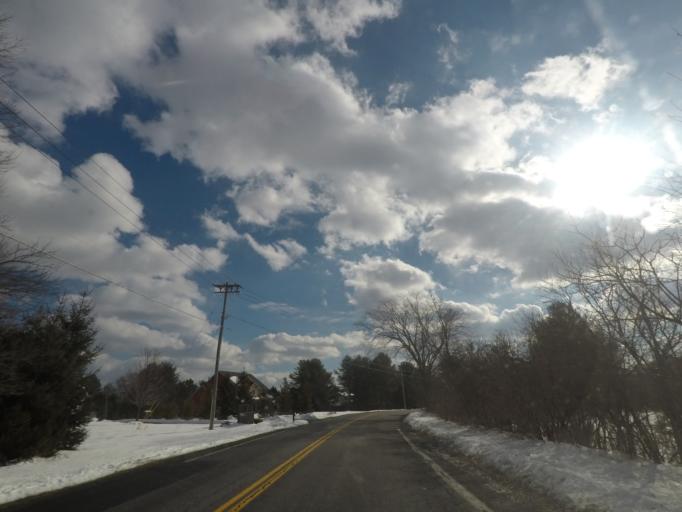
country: US
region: New York
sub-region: Schenectady County
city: Niskayuna
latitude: 42.8308
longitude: -73.8628
